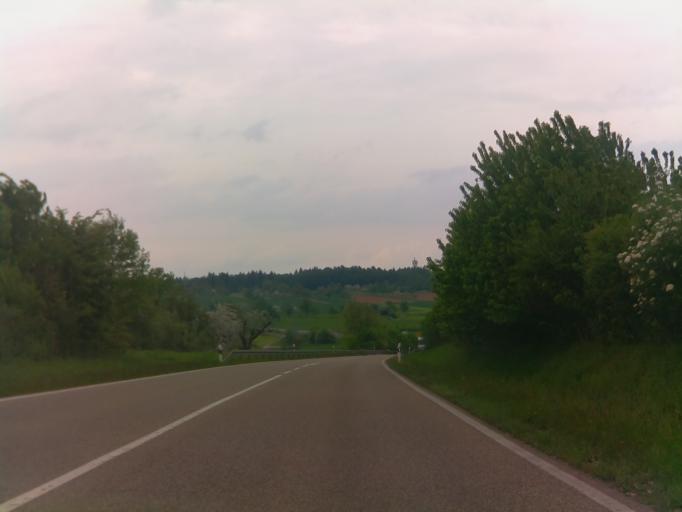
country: DE
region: Baden-Wuerttemberg
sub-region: Tuebingen Region
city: Pliezhausen
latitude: 48.5857
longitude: 9.1700
